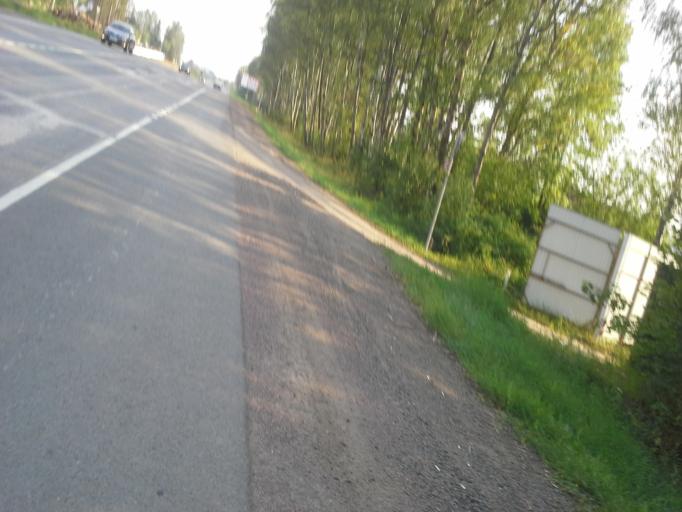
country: RU
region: Moskovskaya
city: Snegiri
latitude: 55.8844
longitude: 36.9437
